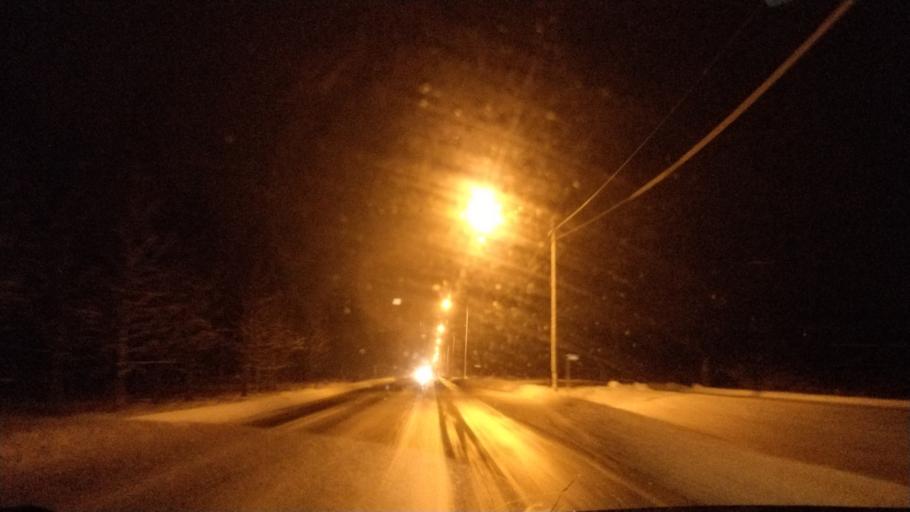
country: FI
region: Lapland
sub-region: Rovaniemi
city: Rovaniemi
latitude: 66.2835
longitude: 25.3389
